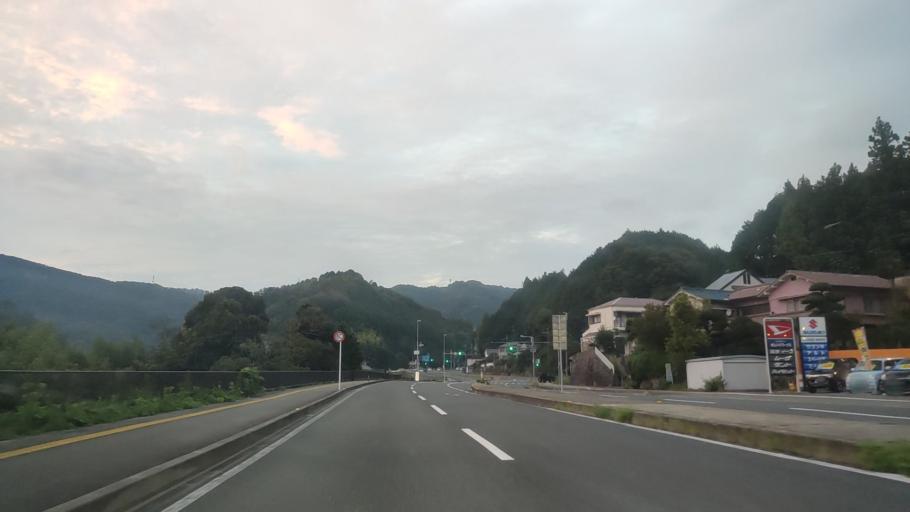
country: JP
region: Wakayama
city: Hashimoto
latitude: 34.3598
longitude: 135.6068
